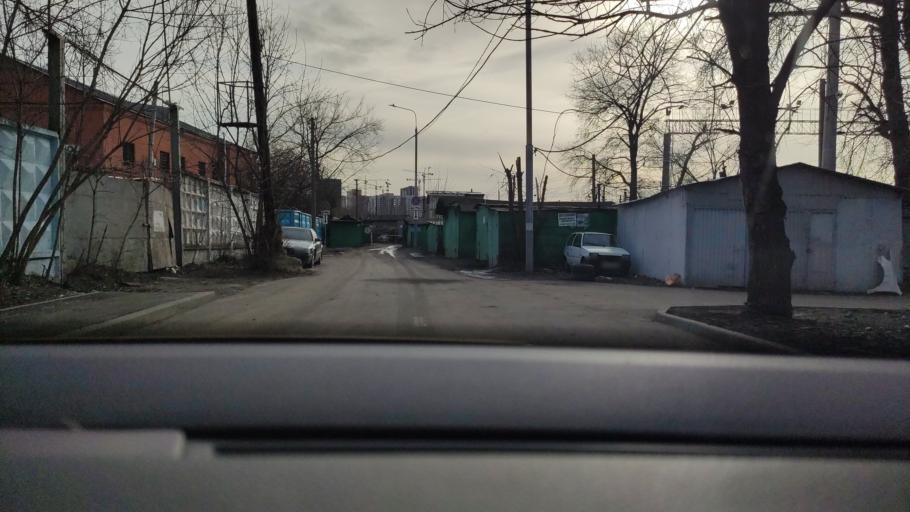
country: RU
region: Moscow
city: Lyublino
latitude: 55.6726
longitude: 37.7322
